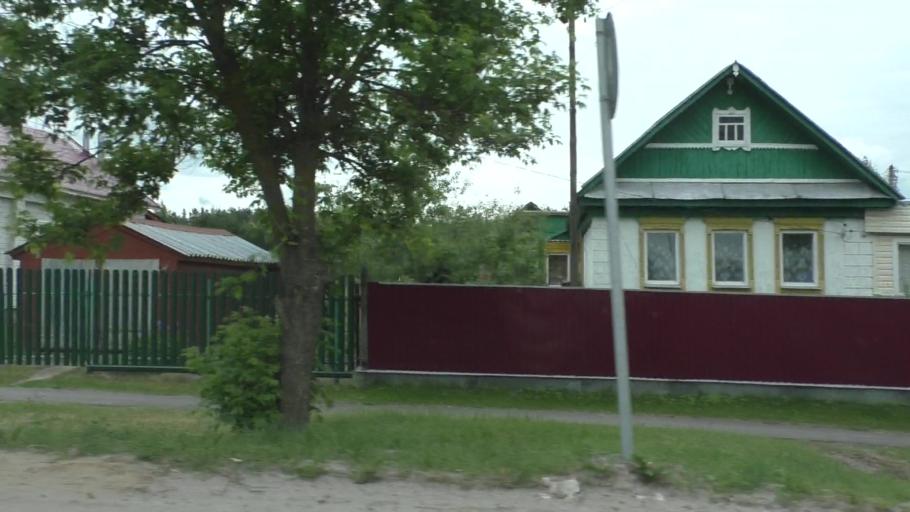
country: RU
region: Moskovskaya
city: Il'inskiy Pogost
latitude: 55.5012
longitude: 38.7990
